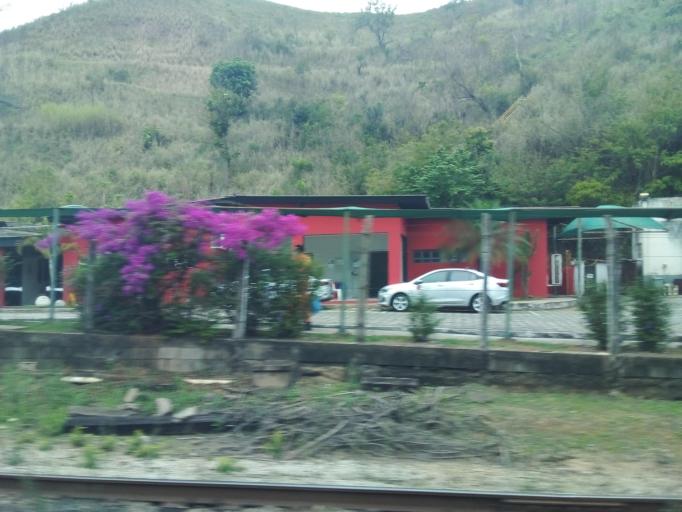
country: BR
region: Minas Gerais
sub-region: Nova Era
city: Nova Era
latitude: -19.7278
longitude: -43.0075
